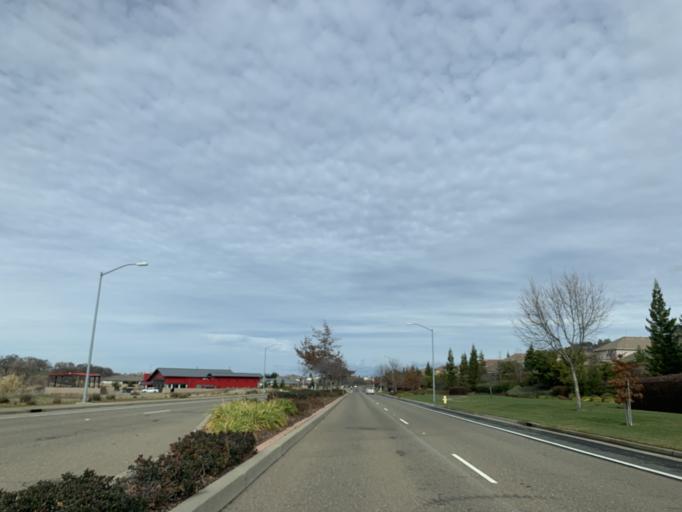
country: US
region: California
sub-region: El Dorado County
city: El Dorado Hills
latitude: 38.6652
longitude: -121.0964
